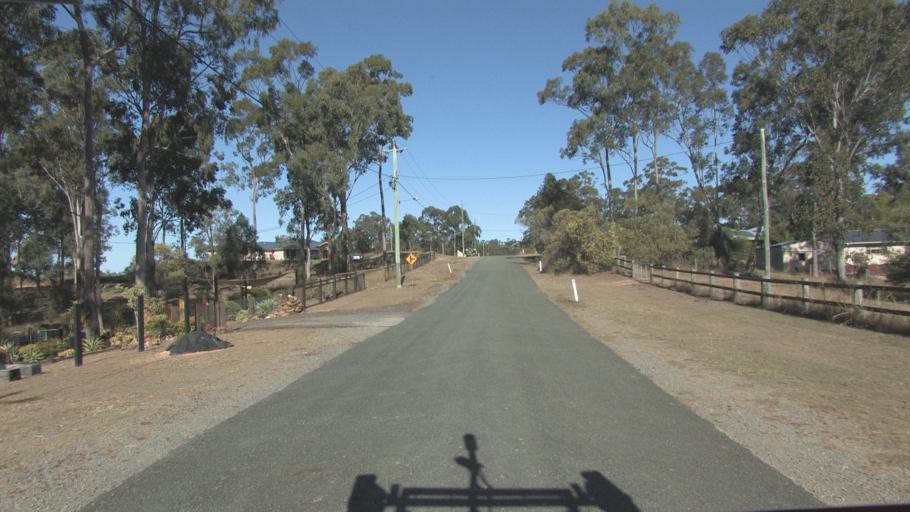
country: AU
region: Queensland
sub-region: Ipswich
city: Springfield Lakes
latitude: -27.7029
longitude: 152.9286
